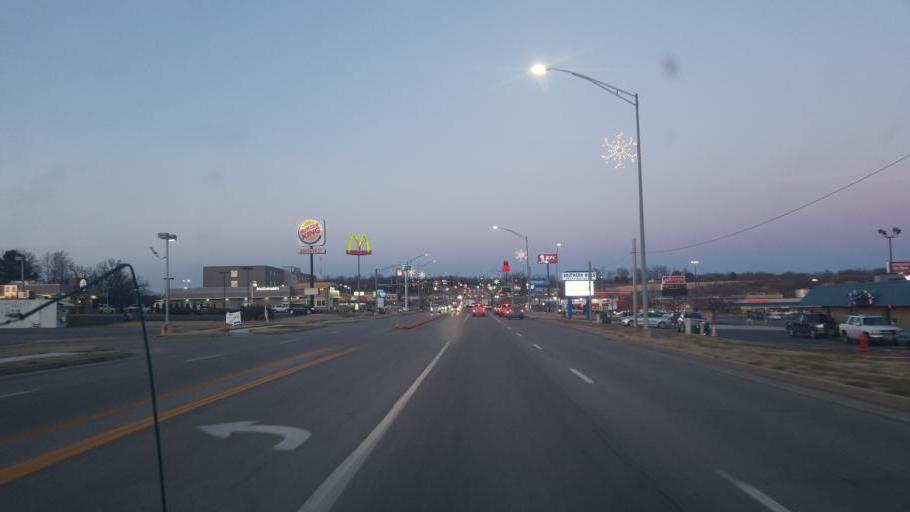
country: US
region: Missouri
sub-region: Howell County
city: West Plains
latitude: 36.7130
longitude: -91.8749
